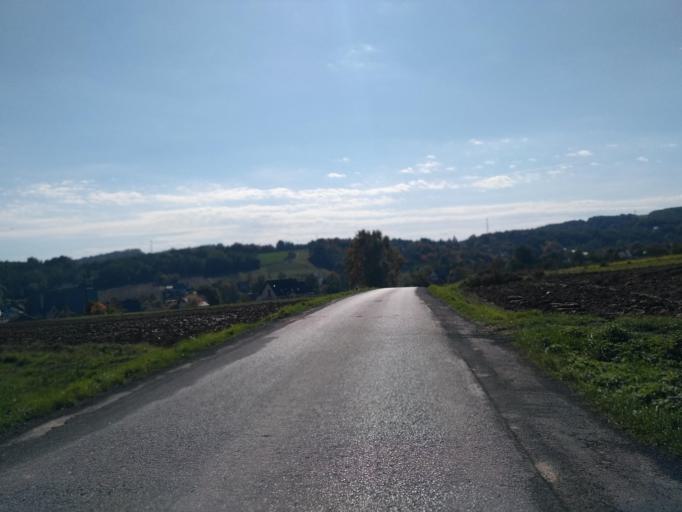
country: PL
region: Subcarpathian Voivodeship
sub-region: Powiat debicki
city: Slotowa
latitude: 49.9492
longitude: 21.2907
